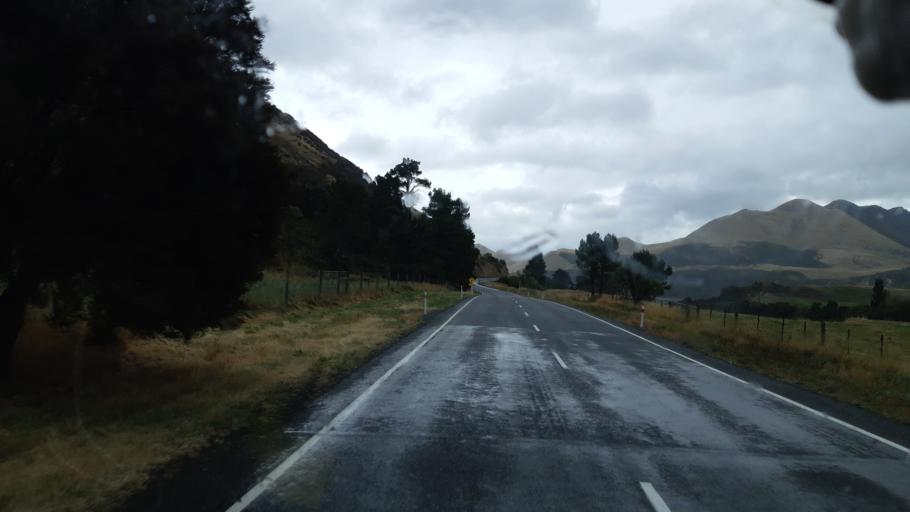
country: NZ
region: Canterbury
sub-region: Hurunui District
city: Amberley
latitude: -42.6352
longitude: 172.7723
